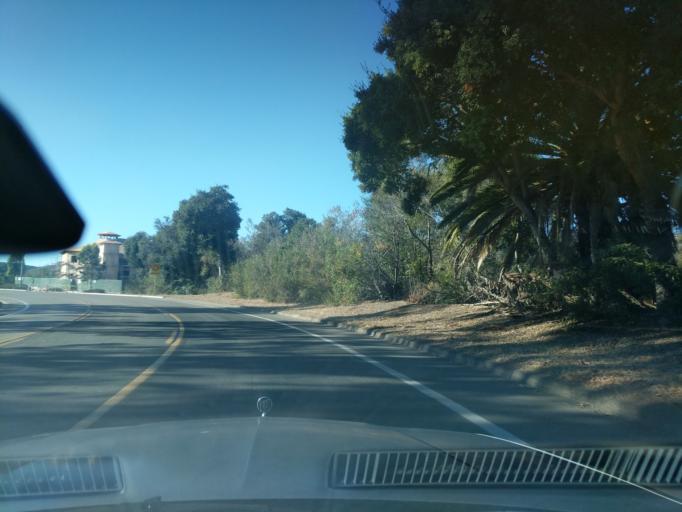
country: US
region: California
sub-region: Santa Barbara County
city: Goleta
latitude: 34.4399
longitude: -119.8515
